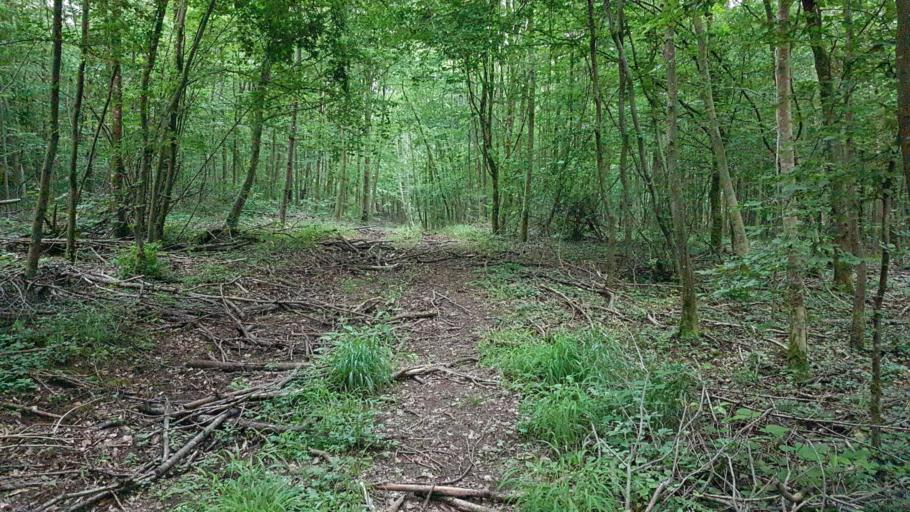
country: FR
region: Lorraine
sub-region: Departement de Meurthe-et-Moselle
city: Hussigny-Godbrange
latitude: 49.5130
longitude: 5.8573
